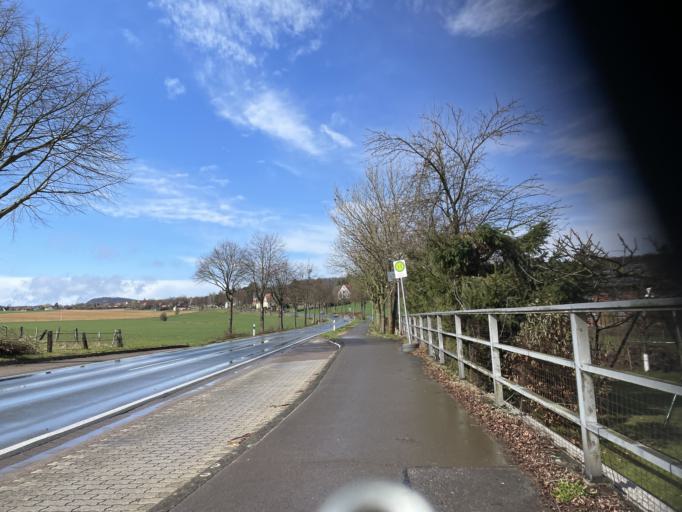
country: DE
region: North Rhine-Westphalia
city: Porta Westfalica
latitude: 52.2261
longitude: 8.9595
